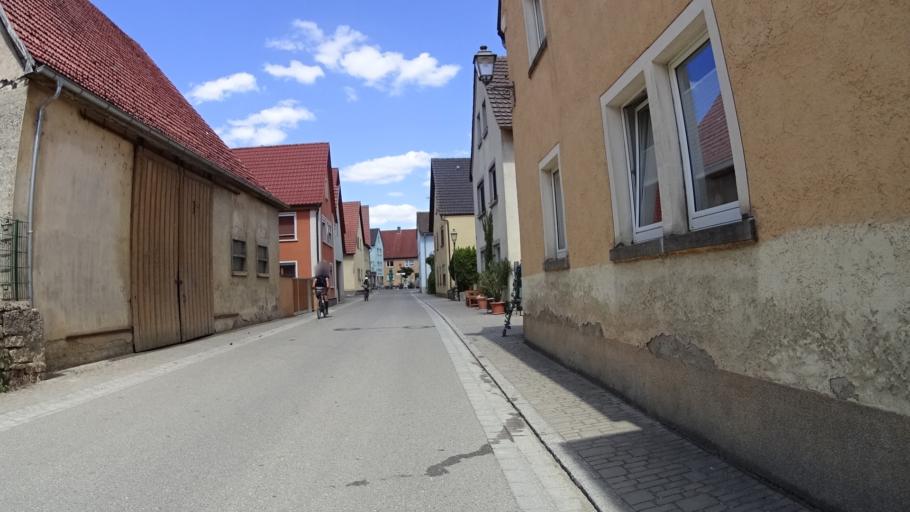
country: DE
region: Bavaria
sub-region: Regierungsbezirk Unterfranken
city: Rottingen
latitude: 49.5095
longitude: 9.9703
